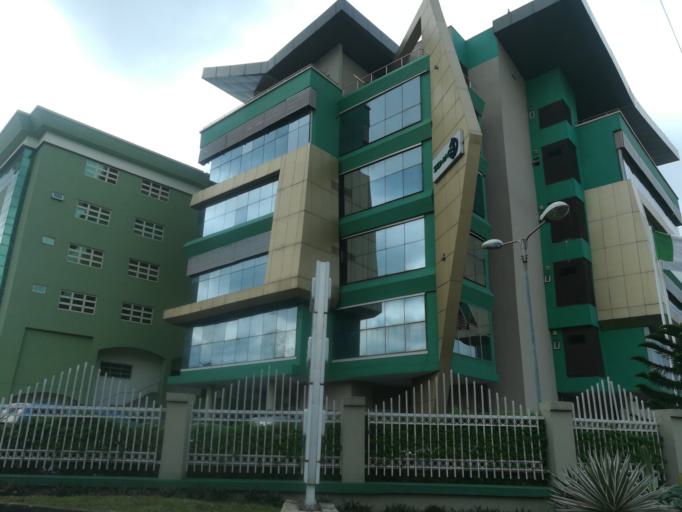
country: NG
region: Lagos
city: Ikeja
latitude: 6.6233
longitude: 3.3599
